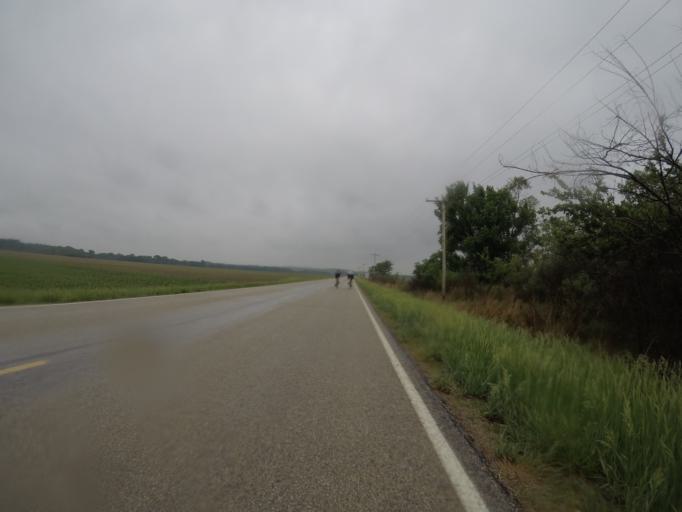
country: US
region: Kansas
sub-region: Pottawatomie County
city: Wamego
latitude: 39.3117
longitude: -96.2215
